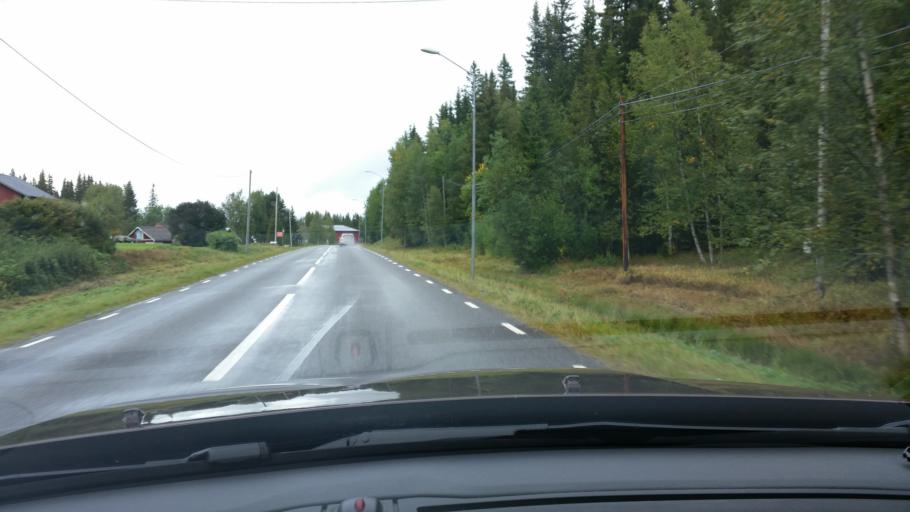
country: NO
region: Nord-Trondelag
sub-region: Lierne
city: Sandvika
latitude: 64.5040
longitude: 14.1574
